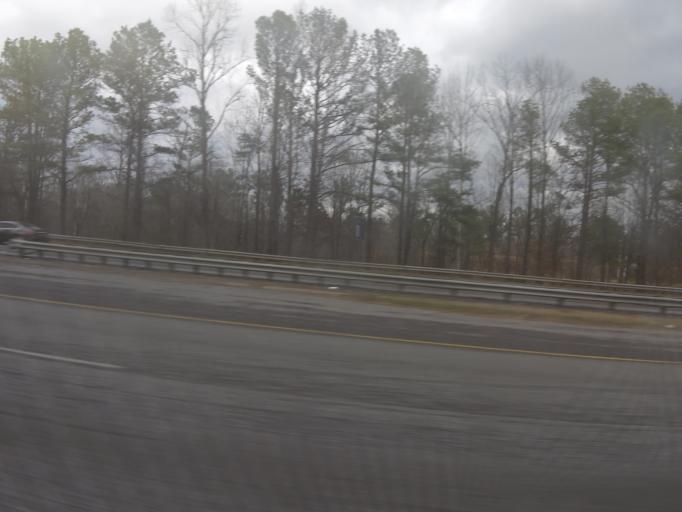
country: US
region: Georgia
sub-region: Whitfield County
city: Dalton
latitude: 34.6652
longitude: -84.9916
